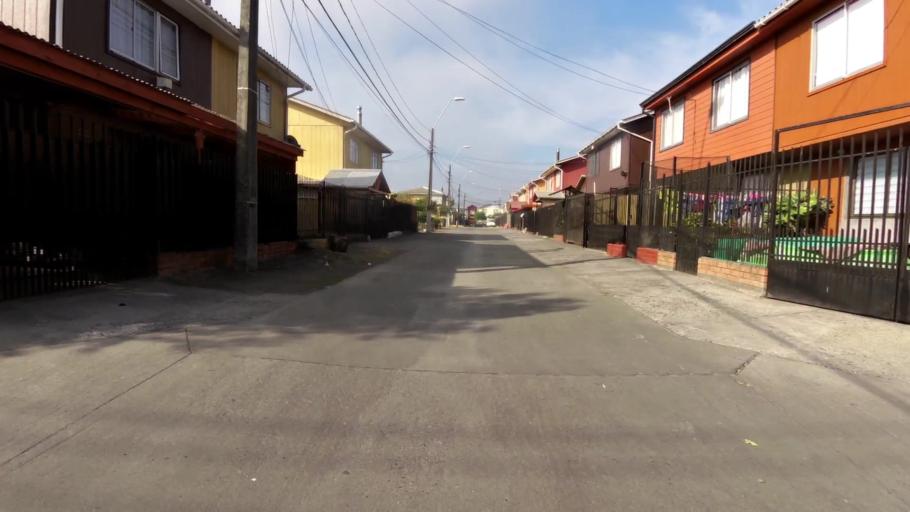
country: CL
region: Biobio
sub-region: Provincia de Concepcion
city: Concepcion
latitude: -36.7959
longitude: -73.1133
